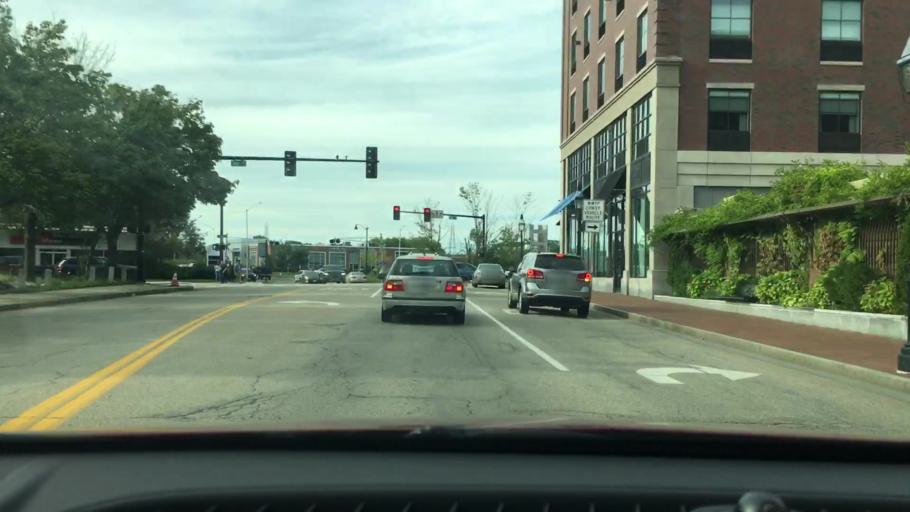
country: US
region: New Hampshire
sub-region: Rockingham County
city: Portsmouth
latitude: 43.0774
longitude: -70.7616
